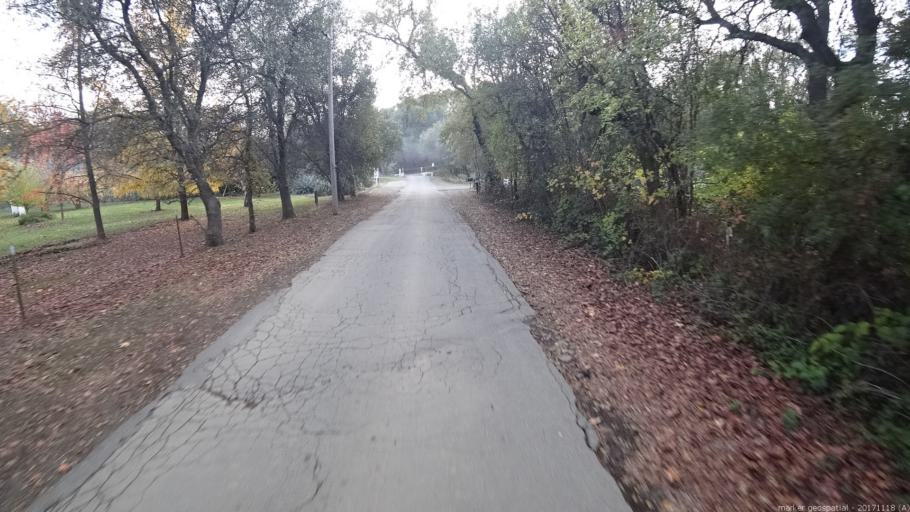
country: US
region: California
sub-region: Shasta County
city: Anderson
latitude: 40.4519
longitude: -122.3241
